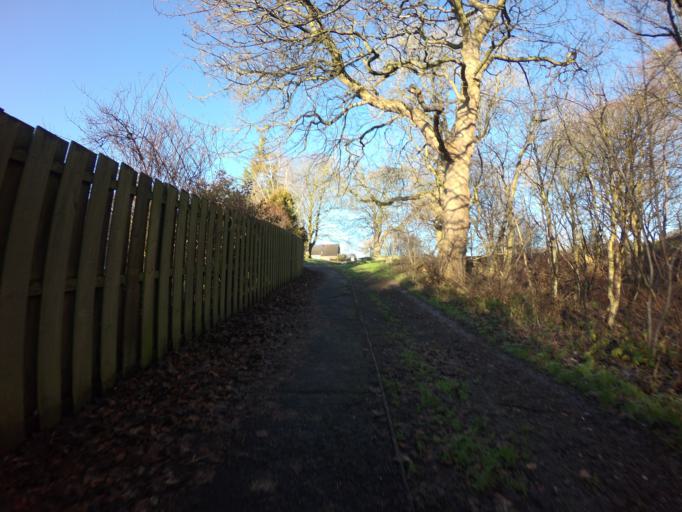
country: GB
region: Scotland
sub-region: West Lothian
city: Livingston
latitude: 55.8872
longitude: -3.5286
